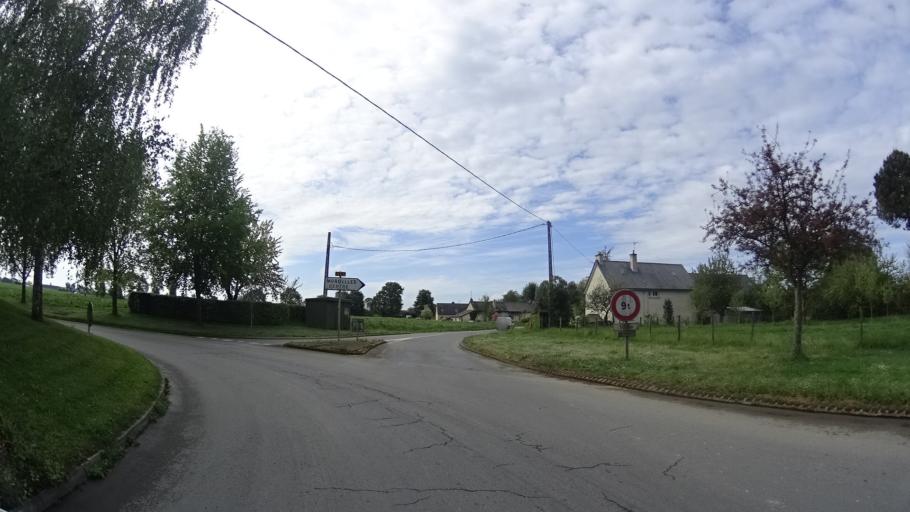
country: FR
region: Brittany
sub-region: Departement d'Ille-et-Vilaine
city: Mordelles
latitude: 48.0857
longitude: -1.8413
